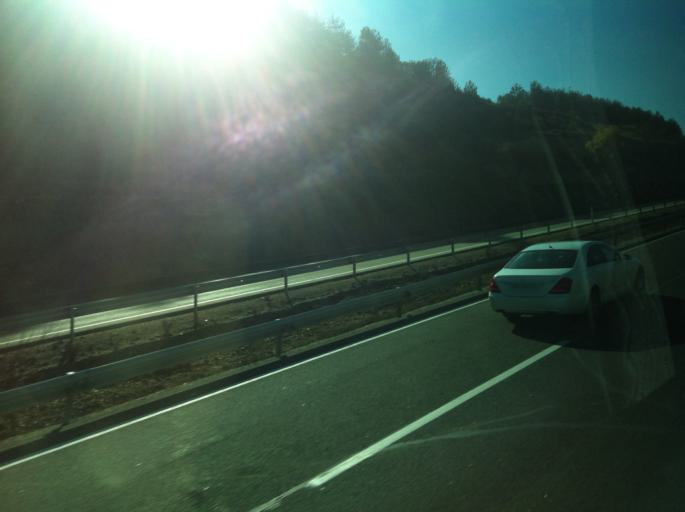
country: ES
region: Castille and Leon
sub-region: Provincia de Burgos
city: Fresno de Rodilla
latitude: 42.4431
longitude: -3.4899
